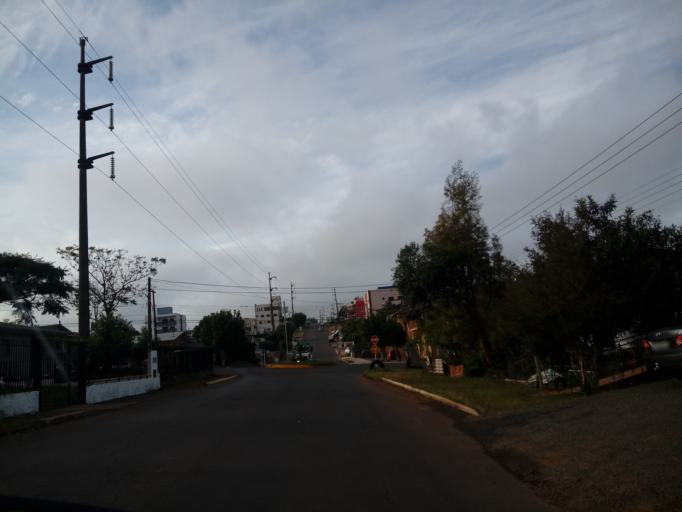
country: BR
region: Santa Catarina
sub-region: Chapeco
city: Chapeco
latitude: -27.0800
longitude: -52.6342
